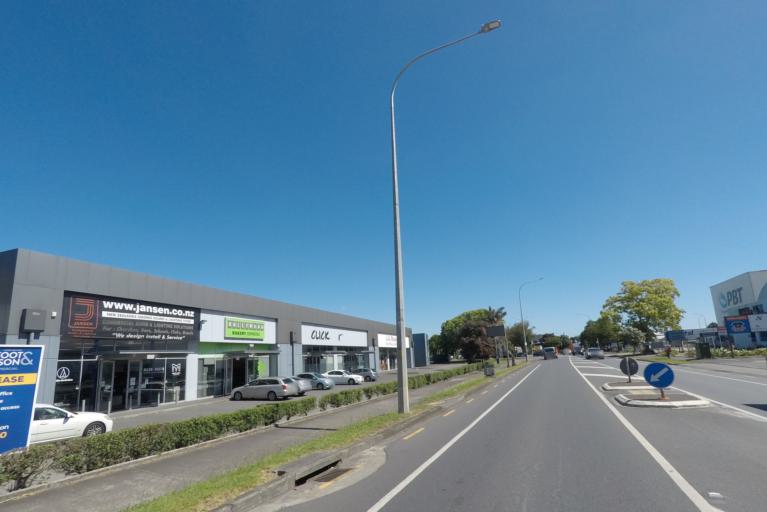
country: NZ
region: Auckland
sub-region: Auckland
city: Rosebank
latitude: -36.8739
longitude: 174.6696
